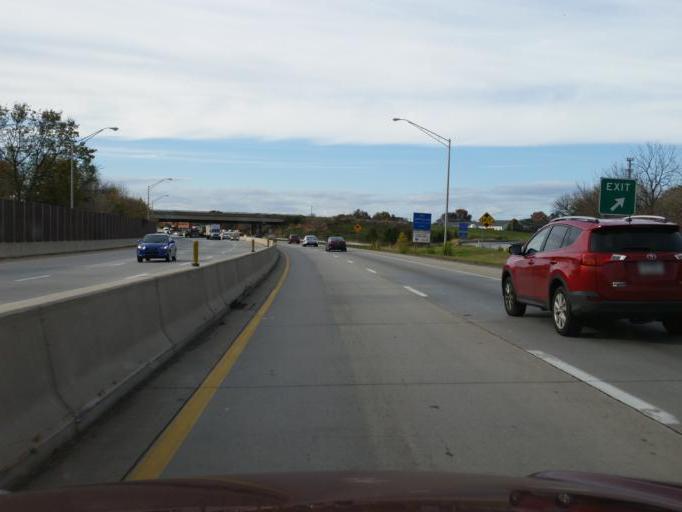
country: US
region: Pennsylvania
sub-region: Lancaster County
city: Lancaster
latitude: 40.0660
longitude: -76.2855
